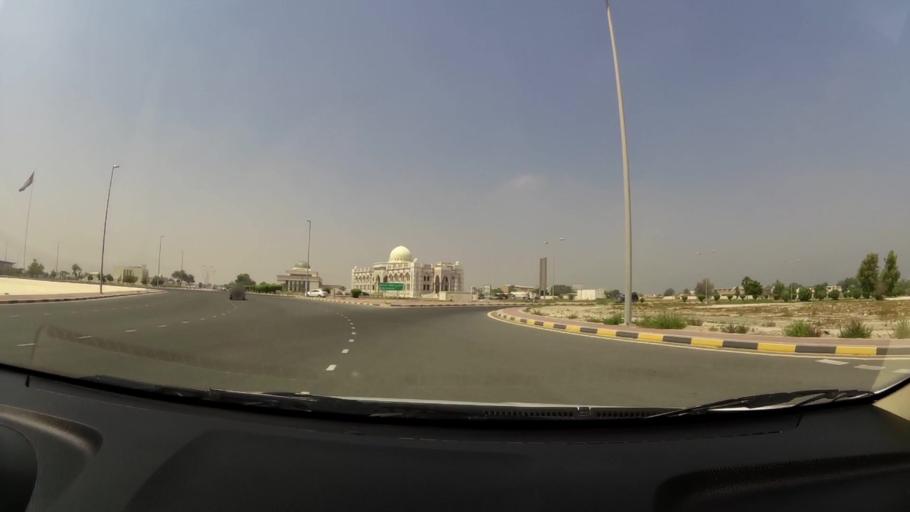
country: AE
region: Umm al Qaywayn
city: Umm al Qaywayn
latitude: 25.5733
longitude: 55.5651
